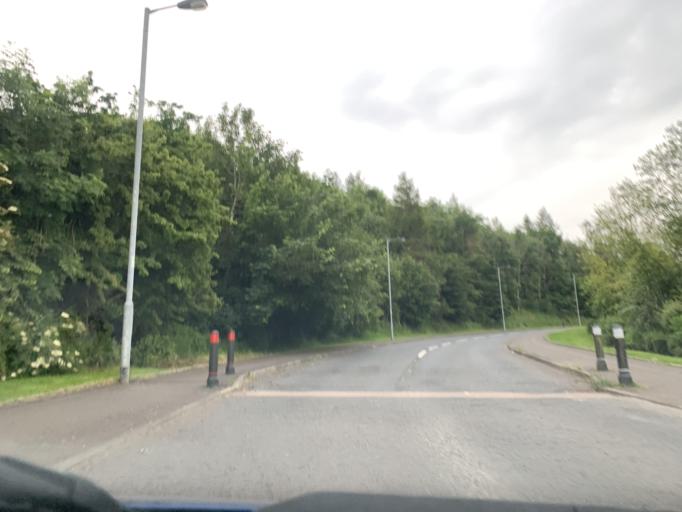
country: GB
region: Scotland
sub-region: East Renfrewshire
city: Newton Mearns
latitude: 55.7716
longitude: -4.3484
